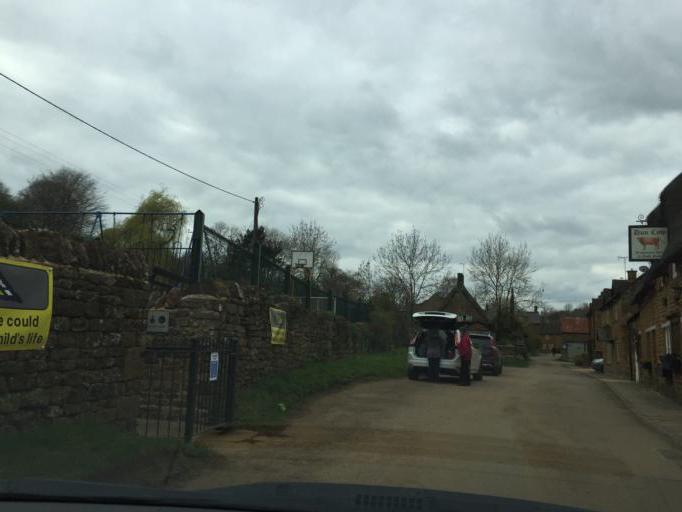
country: GB
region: England
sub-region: Oxfordshire
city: Hanwell
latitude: 52.1012
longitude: -1.4288
